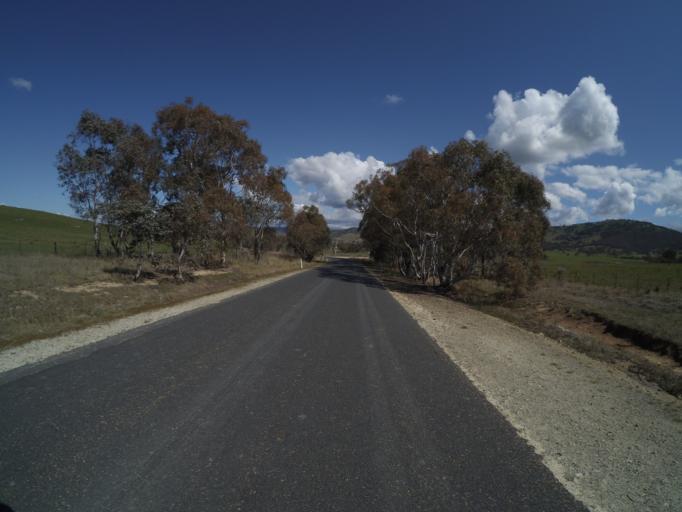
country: AU
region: New South Wales
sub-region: Yass Valley
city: Murrumbateman
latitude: -35.1130
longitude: 148.8652
